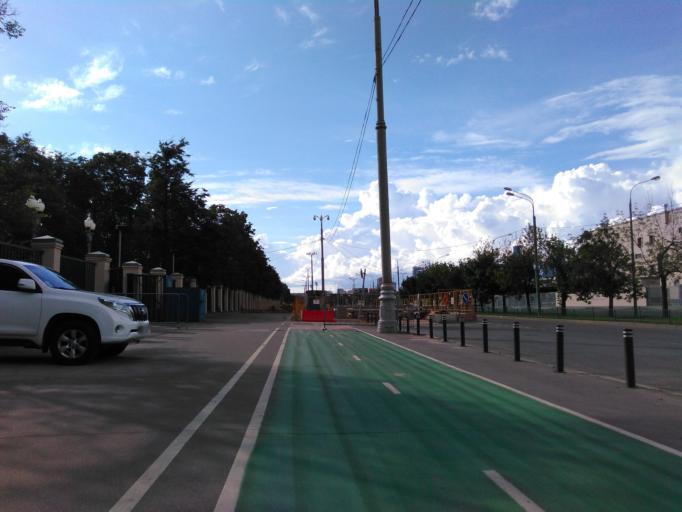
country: RU
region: Moscow
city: Luzhniki
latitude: 55.7198
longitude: 37.5565
